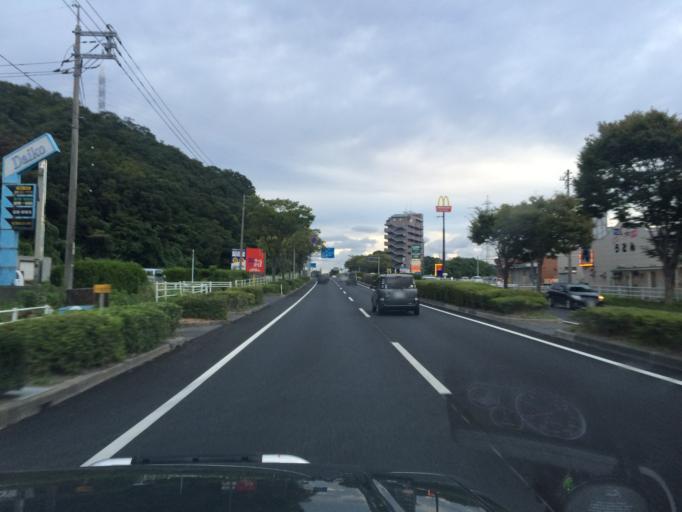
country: JP
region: Tottori
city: Tottori
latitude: 35.4945
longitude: 134.2029
